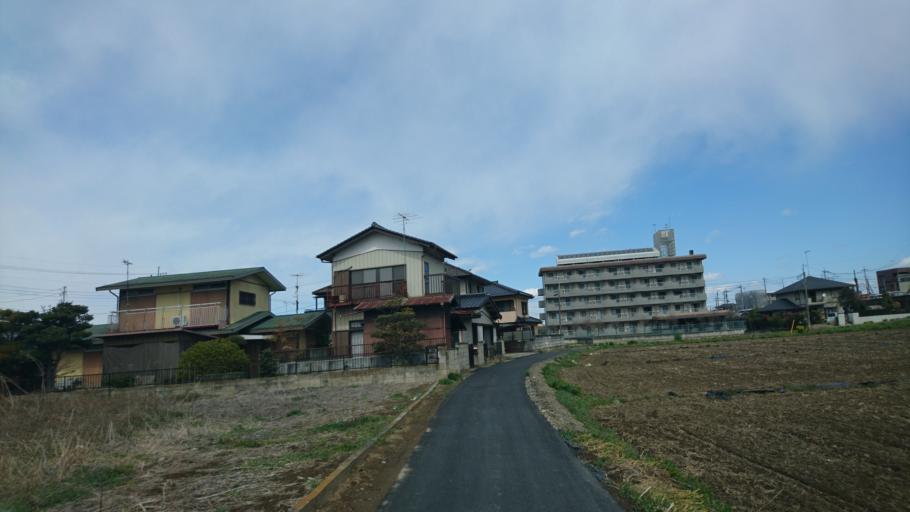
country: JP
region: Ibaraki
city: Yuki
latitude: 36.2944
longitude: 139.9122
